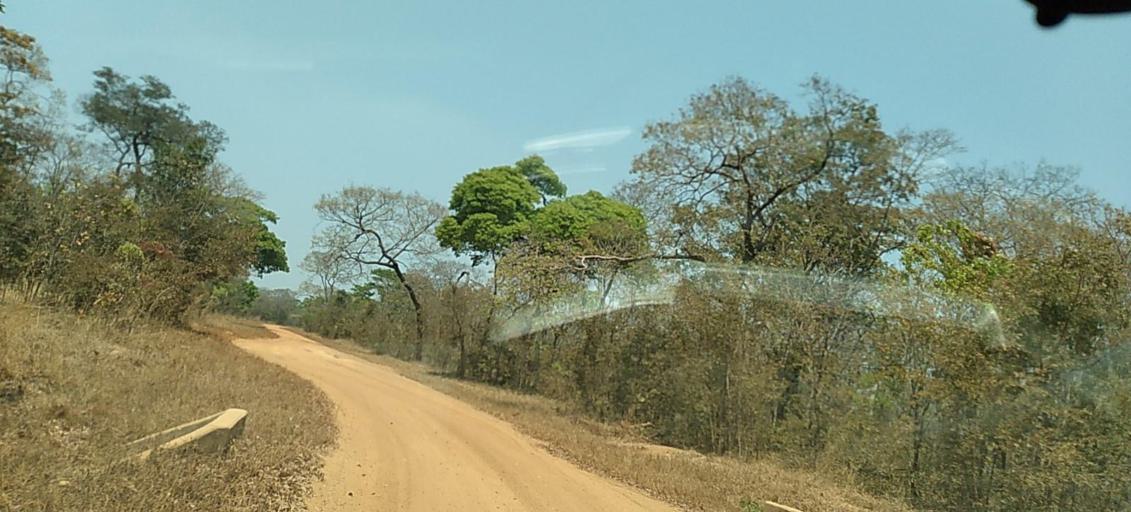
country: ZM
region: Central
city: Mumbwa
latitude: -14.3690
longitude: 26.4794
